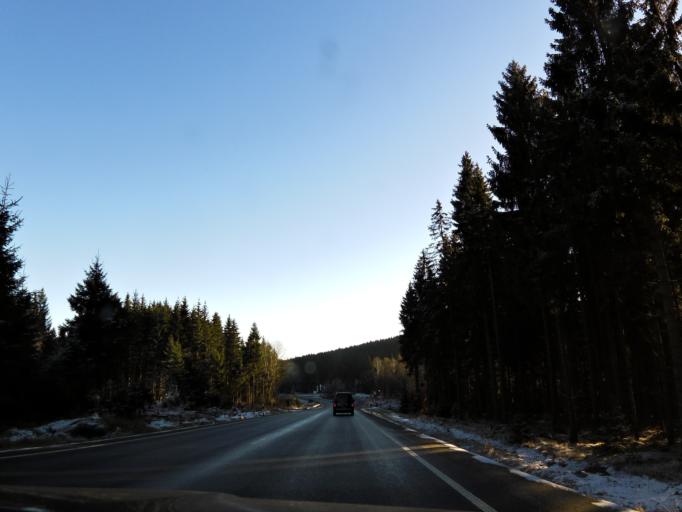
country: DE
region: Bavaria
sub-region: Upper Franconia
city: Fichtelberg
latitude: 50.0400
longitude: 11.8386
